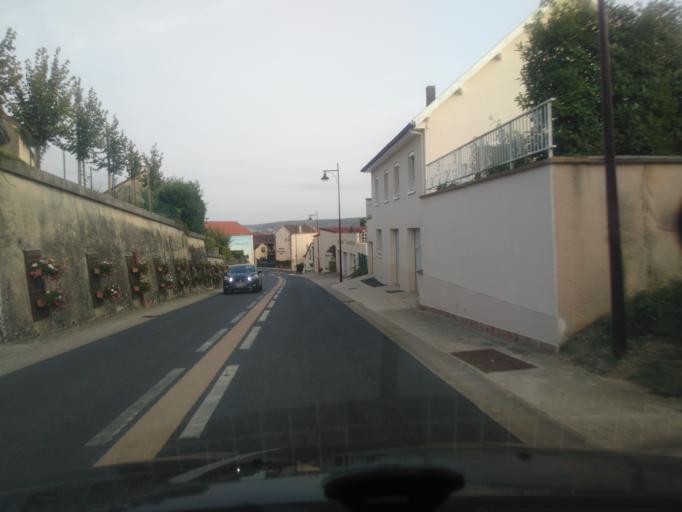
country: FR
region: Champagne-Ardenne
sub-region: Departement de la Marne
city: Damery
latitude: 49.0836
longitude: 3.8382
